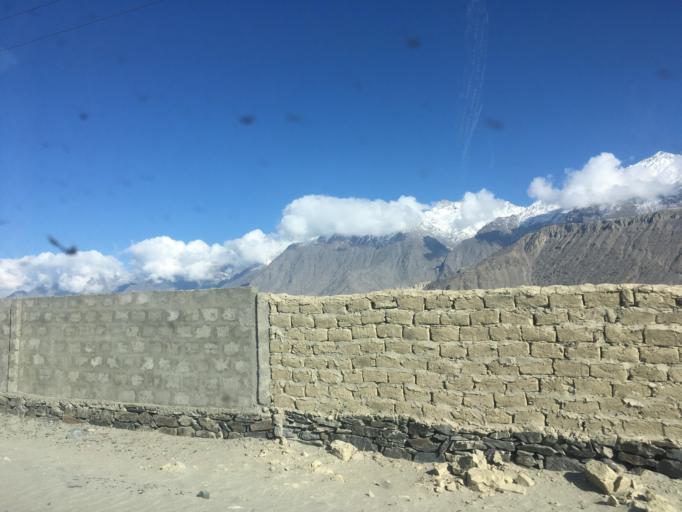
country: PK
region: Gilgit-Baltistan
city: Skardu
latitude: 35.3591
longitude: 75.5345
